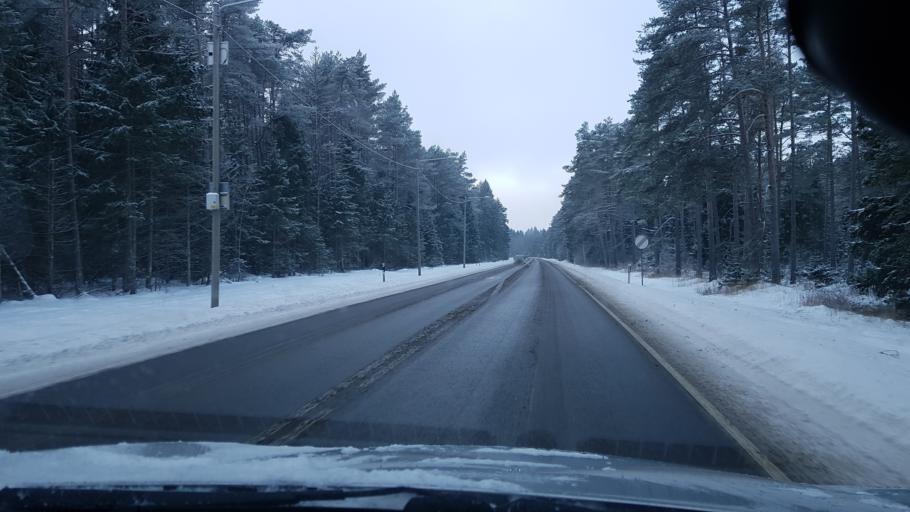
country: EE
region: Harju
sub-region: Keila linn
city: Keila
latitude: 59.3412
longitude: 24.2625
